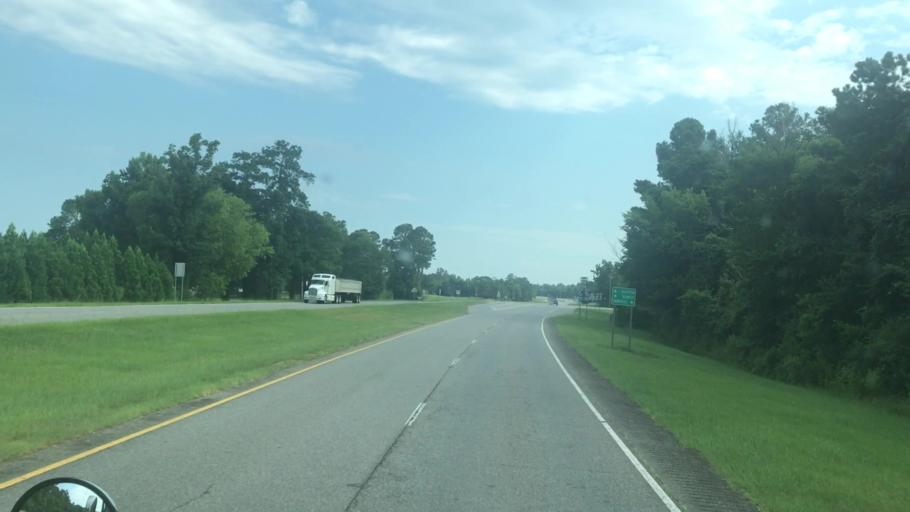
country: US
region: Georgia
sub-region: Early County
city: Blakely
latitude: 31.3733
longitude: -84.9215
